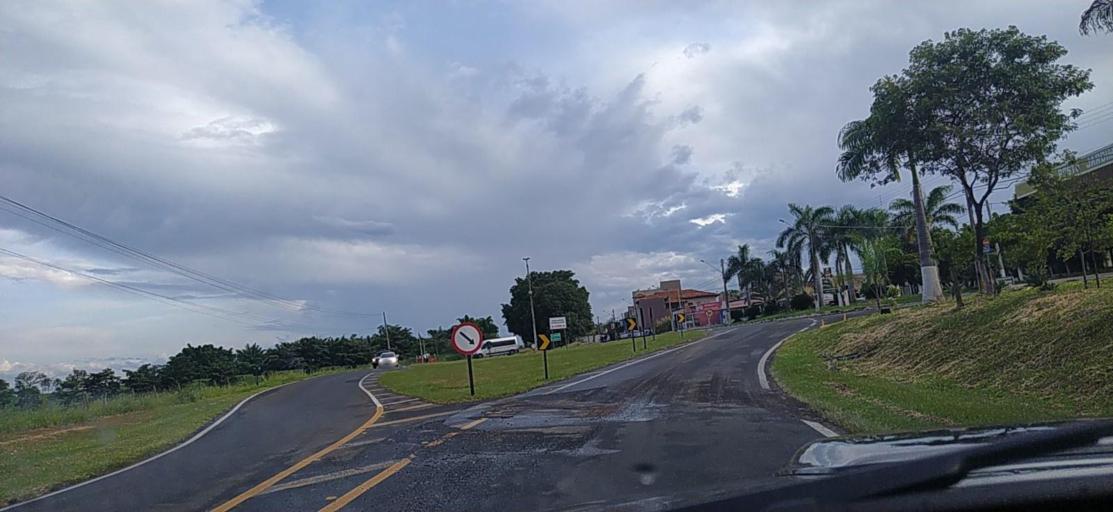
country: BR
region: Sao Paulo
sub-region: Pindorama
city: Pindorama
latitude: -21.1731
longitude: -48.9242
